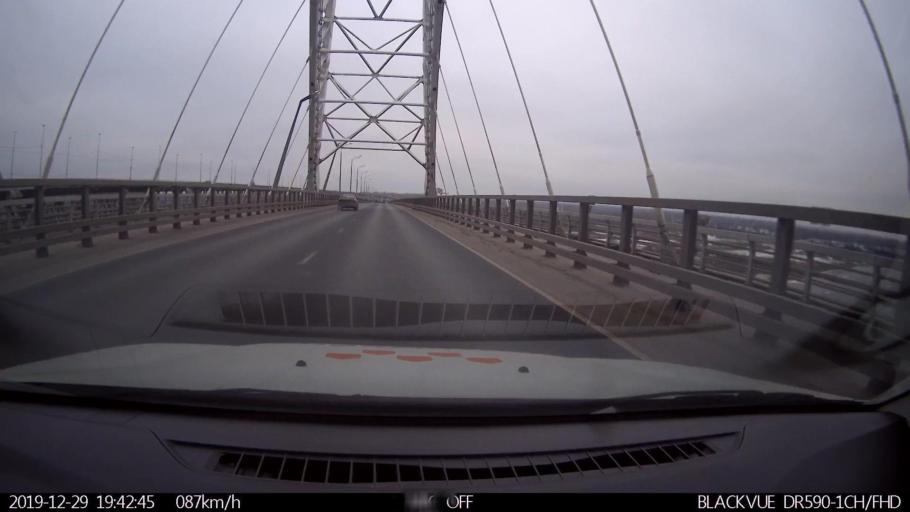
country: RU
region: Nizjnij Novgorod
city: Neklyudovo
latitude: 56.3535
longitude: 43.9255
